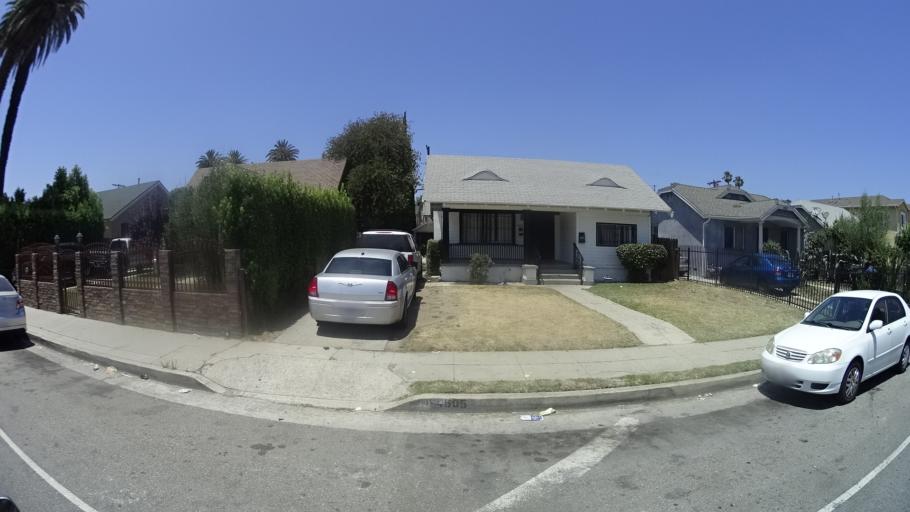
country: US
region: California
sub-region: Los Angeles County
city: View Park-Windsor Hills
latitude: 34.0018
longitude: -118.3182
